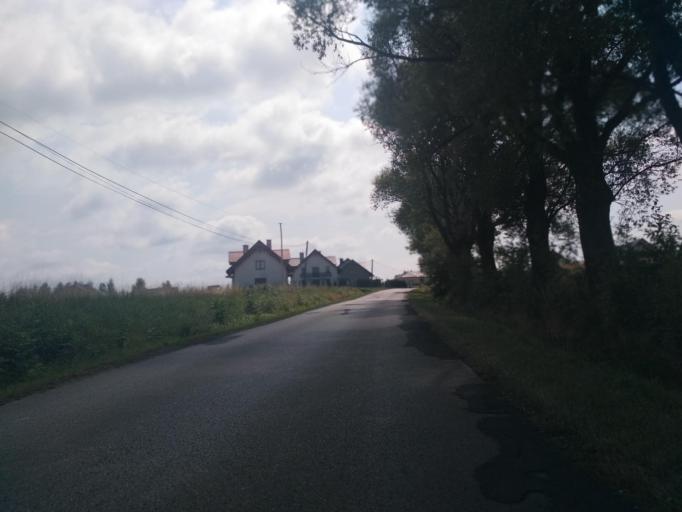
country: PL
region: Subcarpathian Voivodeship
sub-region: Powiat lancucki
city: Kraczkowa
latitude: 50.0340
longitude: 22.1918
